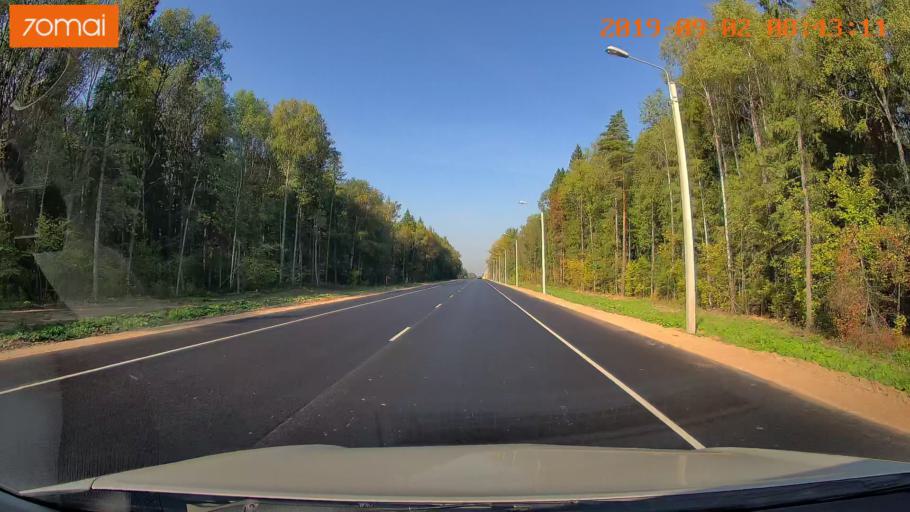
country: RU
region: Kaluga
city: Kudinovo
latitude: 54.9718
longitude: 36.0672
